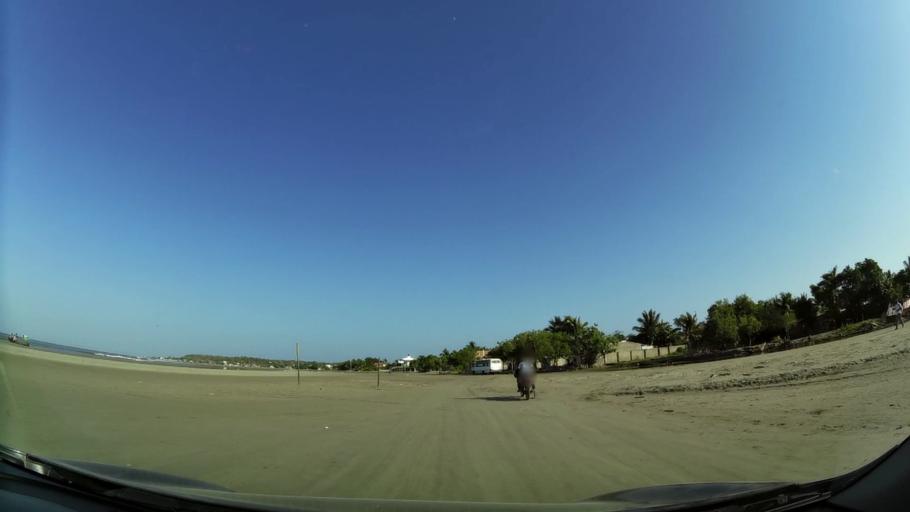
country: CO
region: Bolivar
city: Cartagena
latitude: 10.4888
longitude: -75.4914
